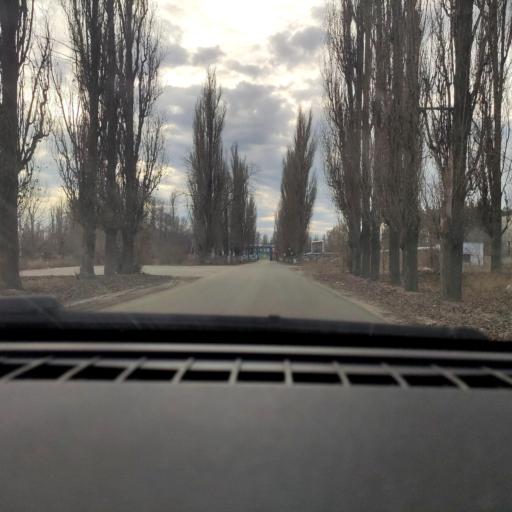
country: RU
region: Voronezj
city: Maslovka
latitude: 51.5992
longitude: 39.2207
